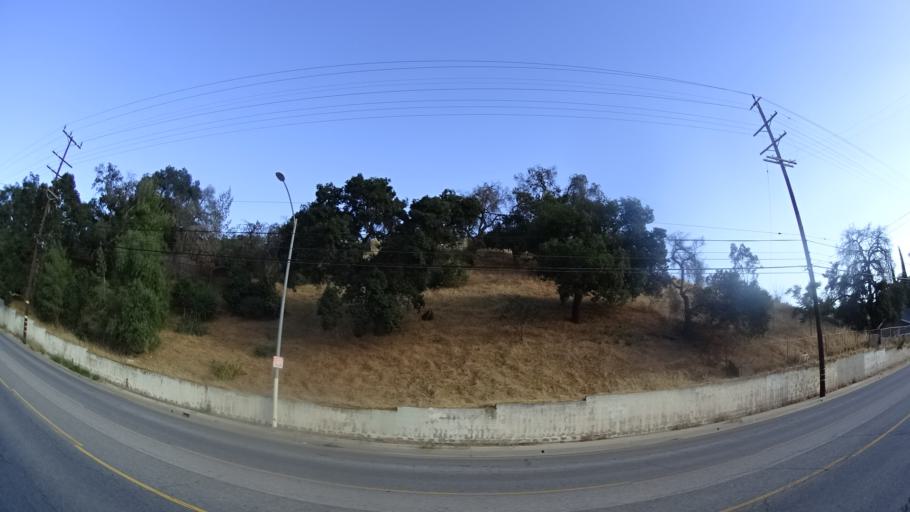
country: US
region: California
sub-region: Los Angeles County
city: North Hollywood
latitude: 34.2471
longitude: -118.3548
